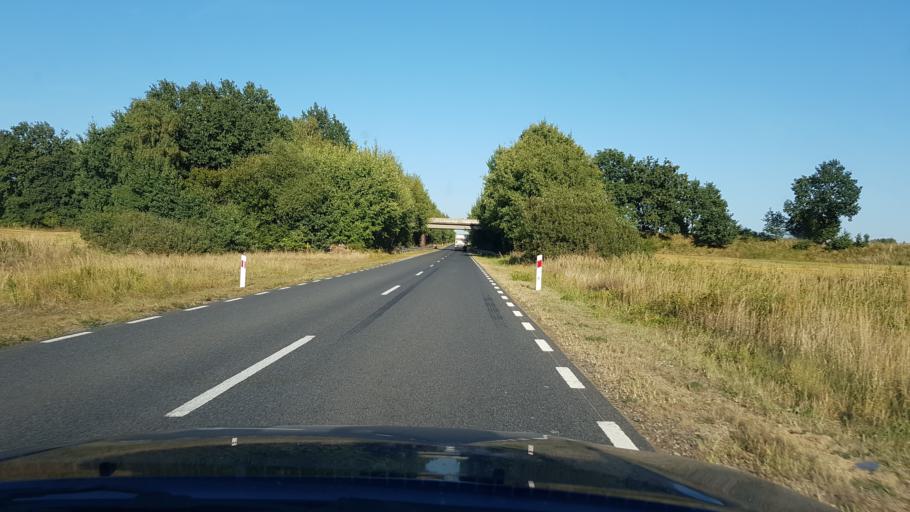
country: PL
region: West Pomeranian Voivodeship
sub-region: Powiat stargardzki
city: Stara Dabrowa
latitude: 53.4331
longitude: 15.1604
